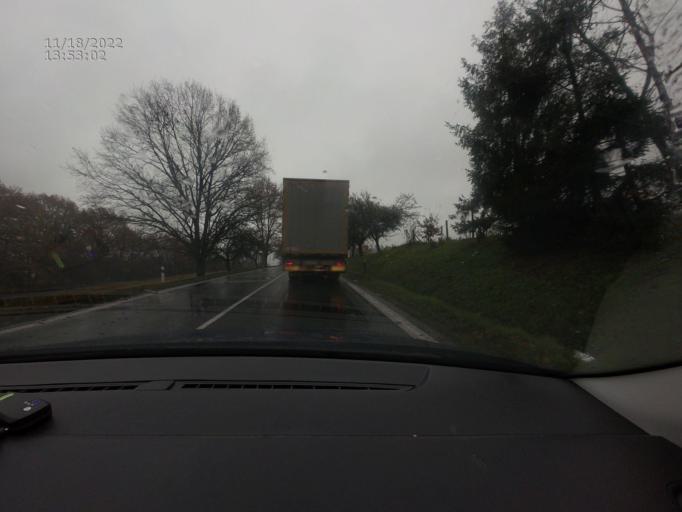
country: CZ
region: Jihocesky
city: Sedlice
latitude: 49.3938
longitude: 13.9169
